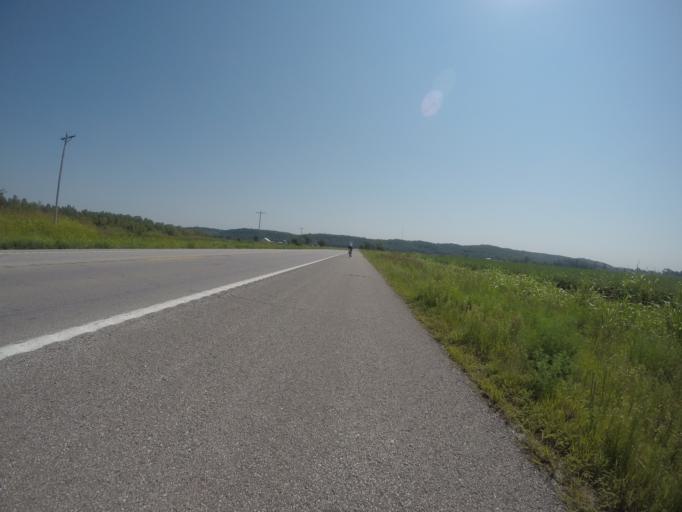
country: US
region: Kansas
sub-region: Atchison County
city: Atchison
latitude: 39.5567
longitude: -95.0645
